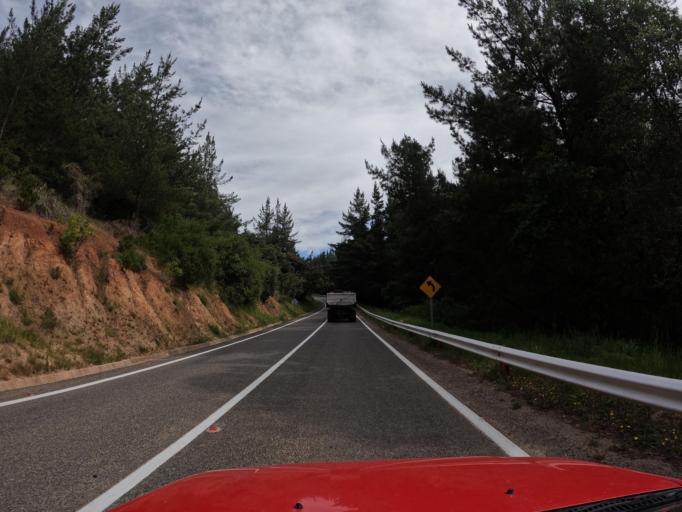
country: CL
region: Maule
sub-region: Provincia de Talca
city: Talca
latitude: -35.2887
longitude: -71.9754
